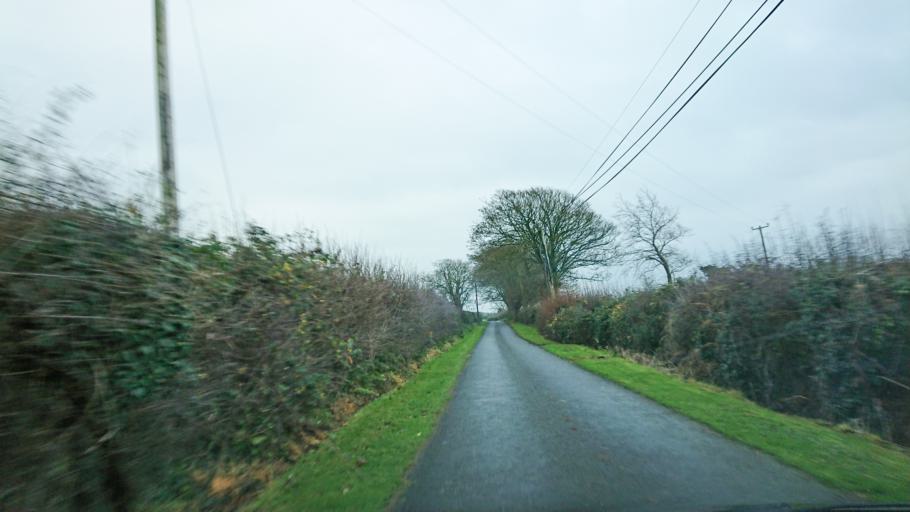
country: IE
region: Munster
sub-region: Waterford
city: Dunmore East
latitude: 52.2052
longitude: -6.9971
